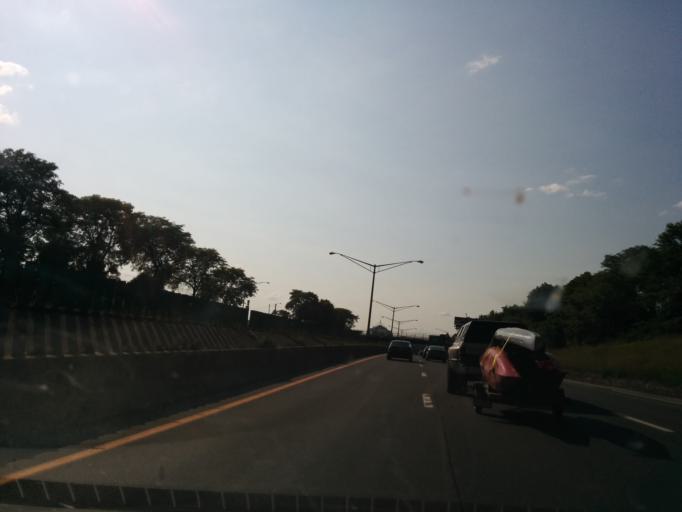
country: US
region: New York
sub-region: Onondaga County
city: Syracuse
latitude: 43.0654
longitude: -76.1612
